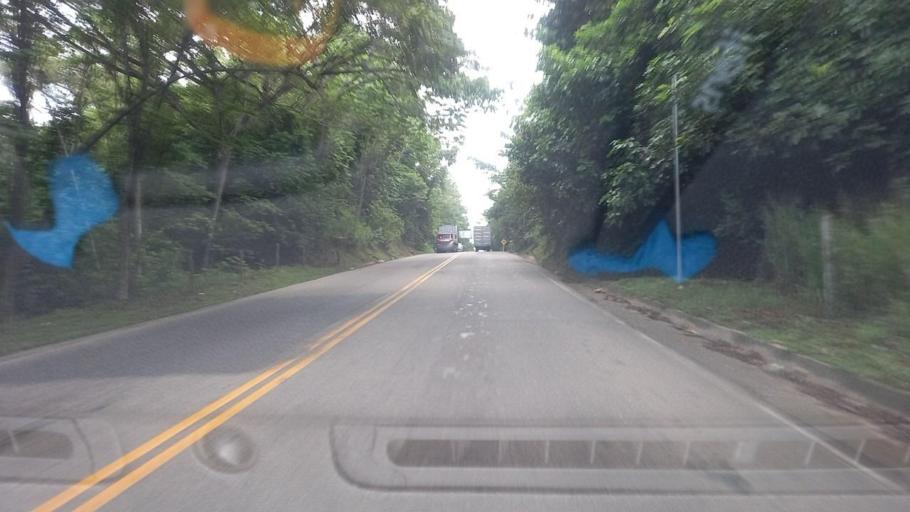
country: CO
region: Santander
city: Sabana de Torres
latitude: 7.1294
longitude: -73.5671
